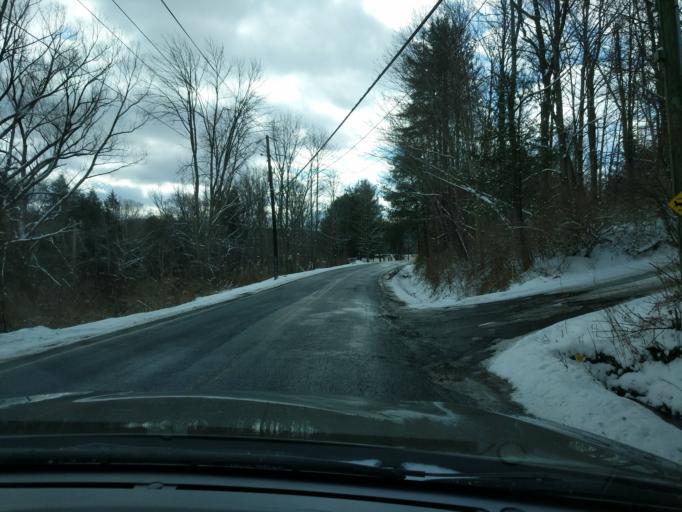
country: US
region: New York
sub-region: Tompkins County
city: East Ithaca
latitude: 42.3923
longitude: -76.3758
